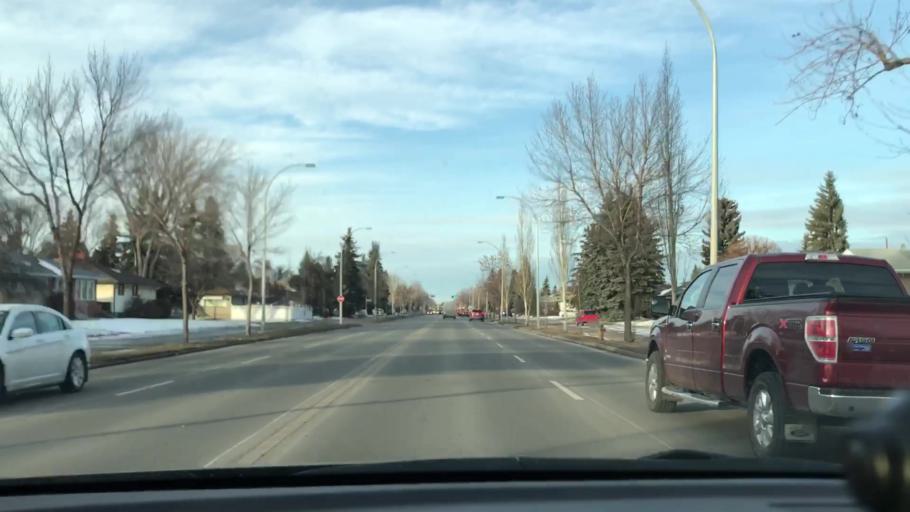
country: CA
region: Alberta
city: Edmonton
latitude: 53.5297
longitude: -113.4429
